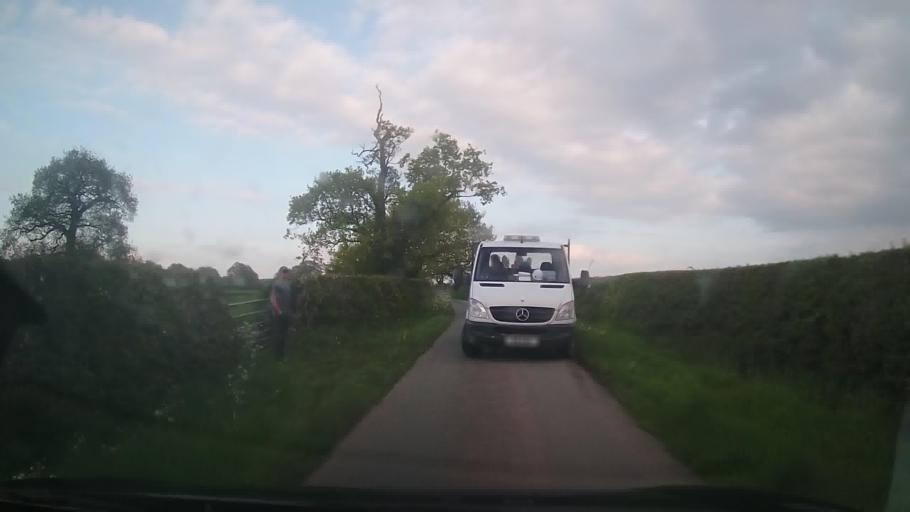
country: GB
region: England
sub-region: Shropshire
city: Ellesmere
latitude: 52.9308
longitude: -2.8391
